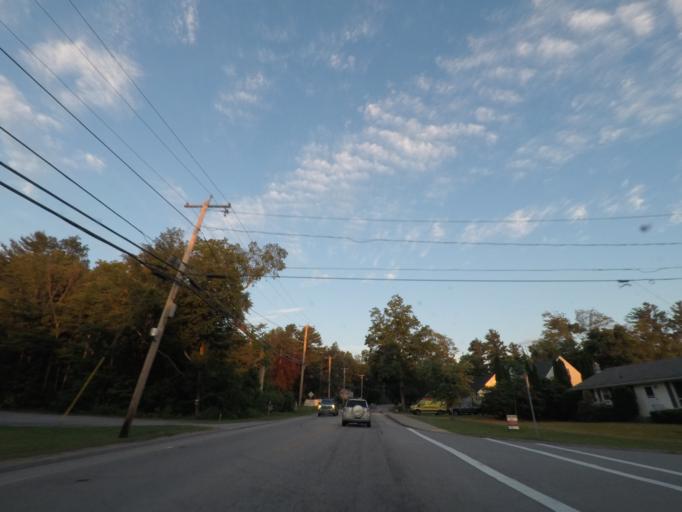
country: US
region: Massachusetts
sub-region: Worcester County
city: Sturbridge
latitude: 42.1002
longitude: -72.0744
